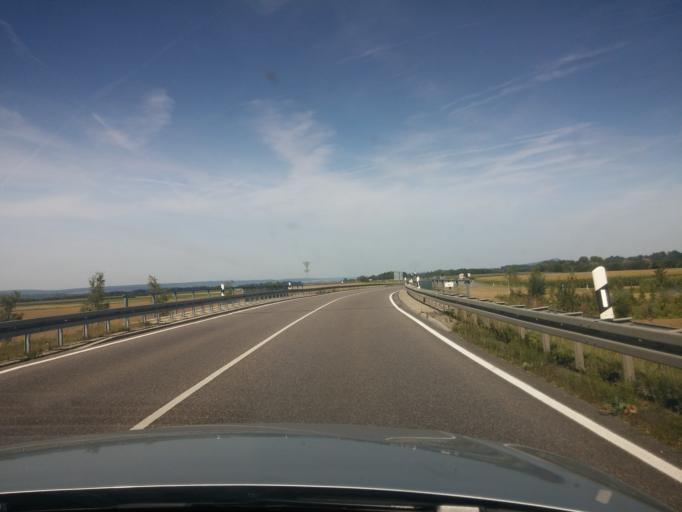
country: DE
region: Baden-Wuerttemberg
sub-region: Tuebingen Region
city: Herbertingen
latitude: 48.0664
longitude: 9.4422
